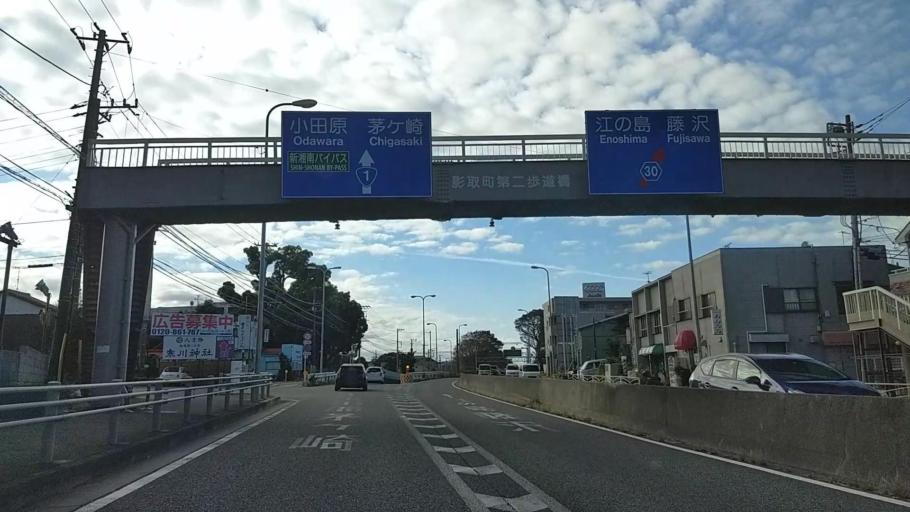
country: JP
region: Kanagawa
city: Fujisawa
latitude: 35.3640
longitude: 139.4973
